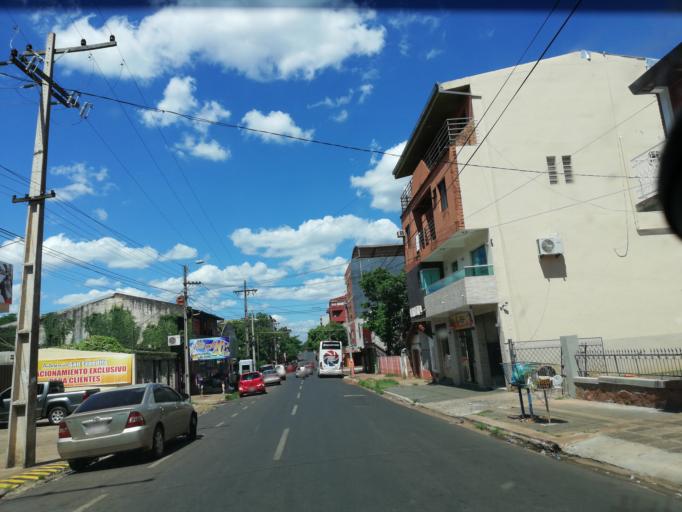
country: PY
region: Itapua
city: Encarnacion
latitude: -27.3394
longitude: -55.8633
